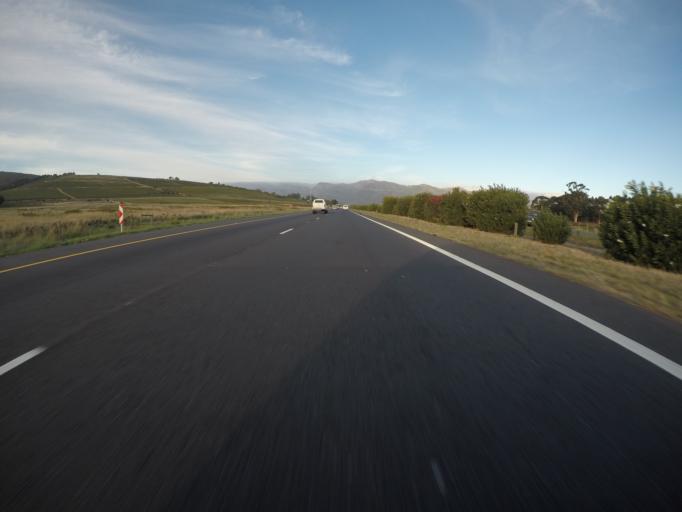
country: ZA
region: Western Cape
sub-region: Cape Winelands District Municipality
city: Paarl
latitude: -33.7869
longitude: 18.9296
